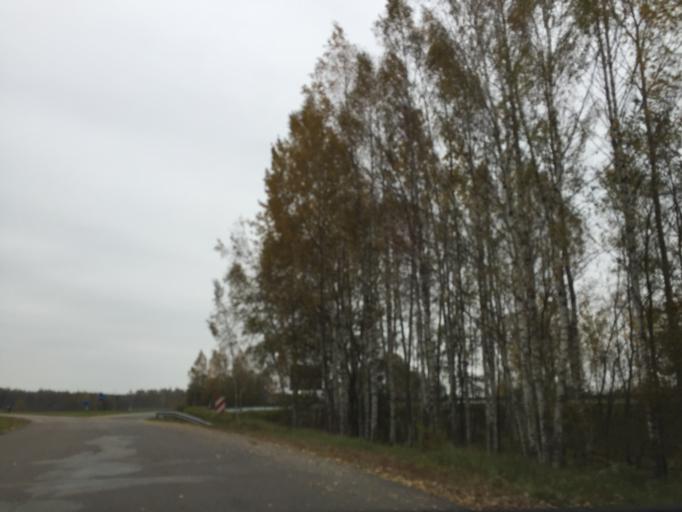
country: LV
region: Marupe
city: Marupe
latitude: 56.8367
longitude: 24.0313
